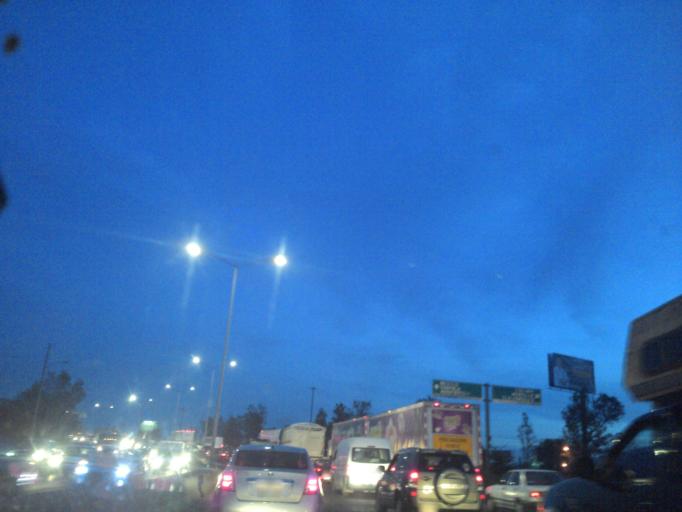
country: MX
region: Jalisco
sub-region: Tlajomulco de Zuniga
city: La Tijera
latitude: 20.6163
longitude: -103.4288
